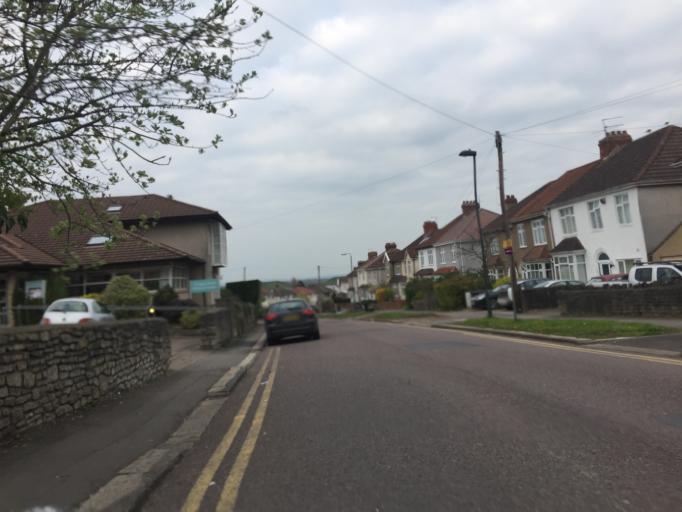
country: GB
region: England
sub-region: South Gloucestershire
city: Stoke Gifford
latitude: 51.5108
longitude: -2.5716
